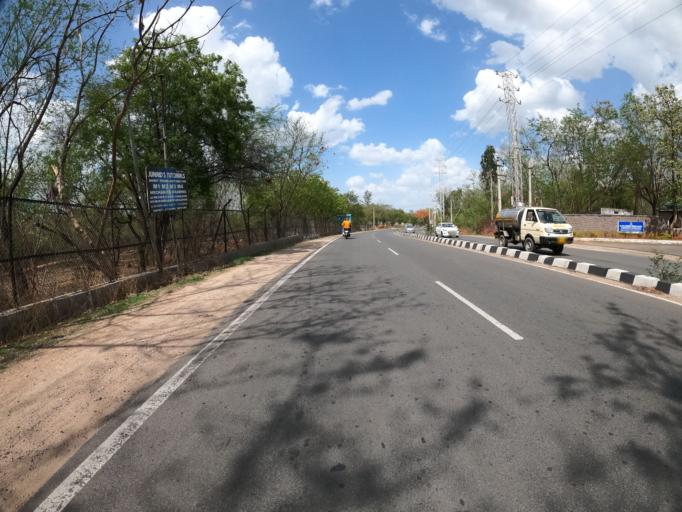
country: IN
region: Telangana
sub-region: Rangareddi
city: Sriramnagar
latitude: 17.3539
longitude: 78.3338
